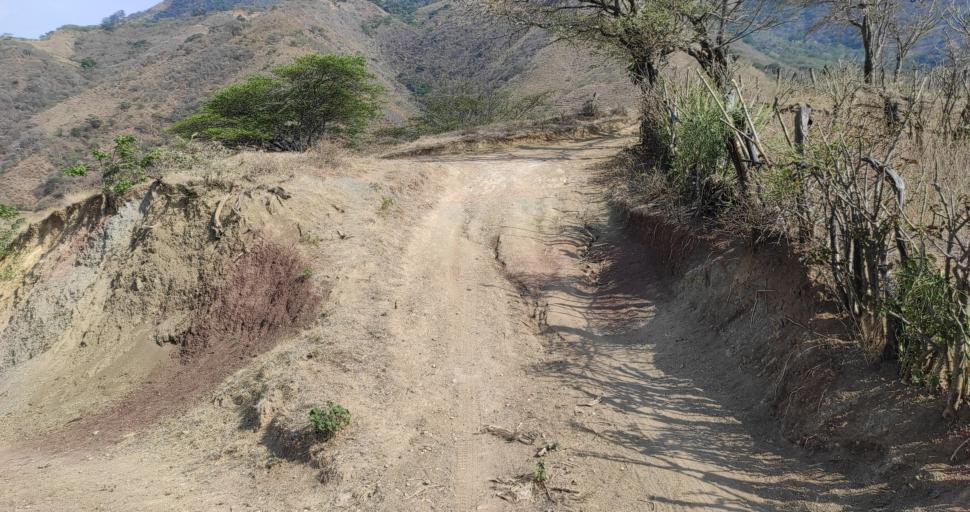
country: EC
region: Loja
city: Catacocha
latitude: -4.0022
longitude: -79.7145
